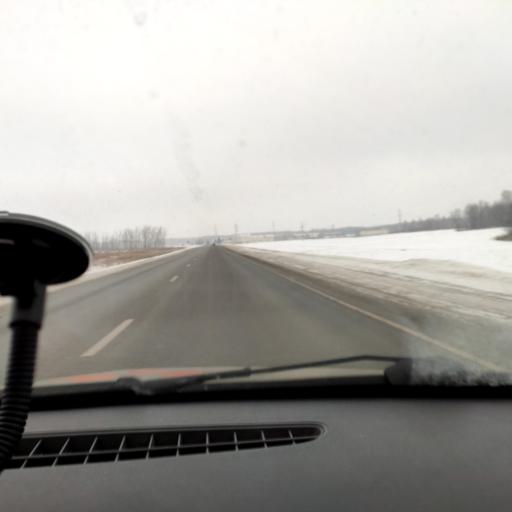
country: RU
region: Bashkortostan
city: Mikhaylovka
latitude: 54.8271
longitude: 55.8268
